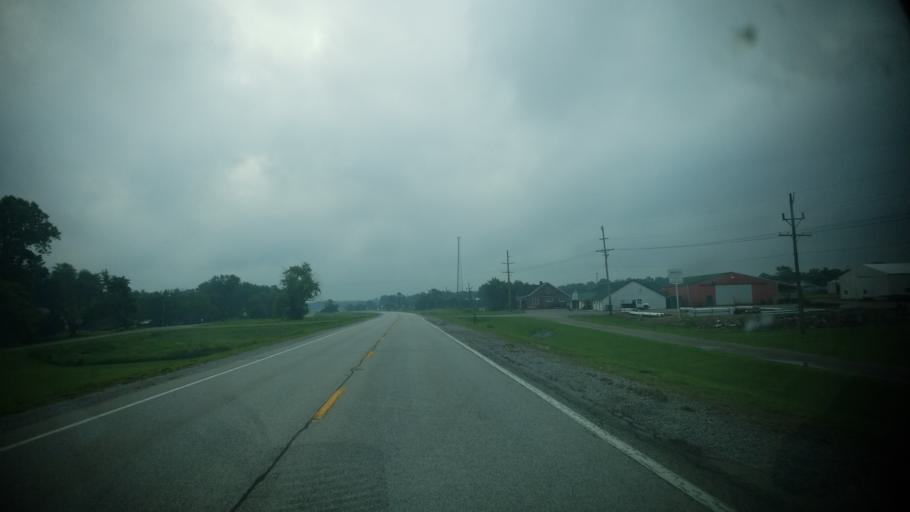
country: US
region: Illinois
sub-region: Clay County
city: Flora
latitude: 38.6780
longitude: -88.3677
